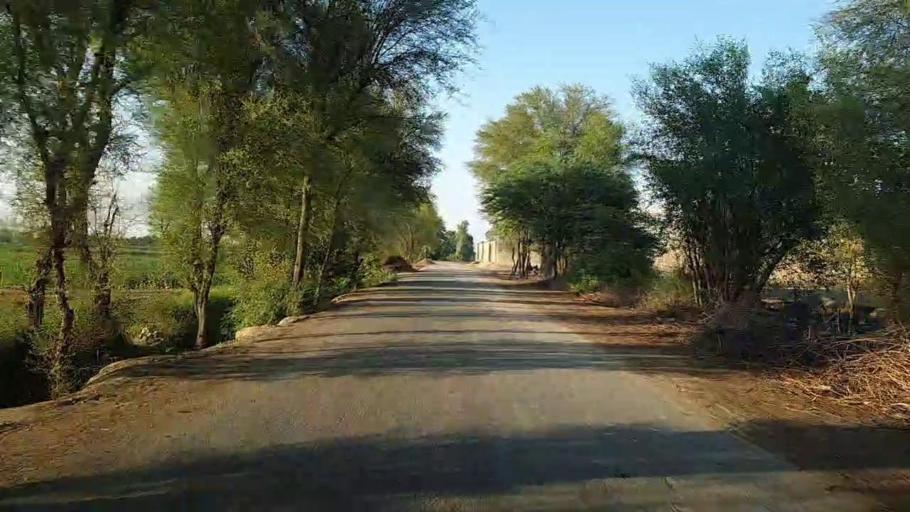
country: PK
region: Sindh
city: Bhan
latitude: 26.5806
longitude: 67.7601
